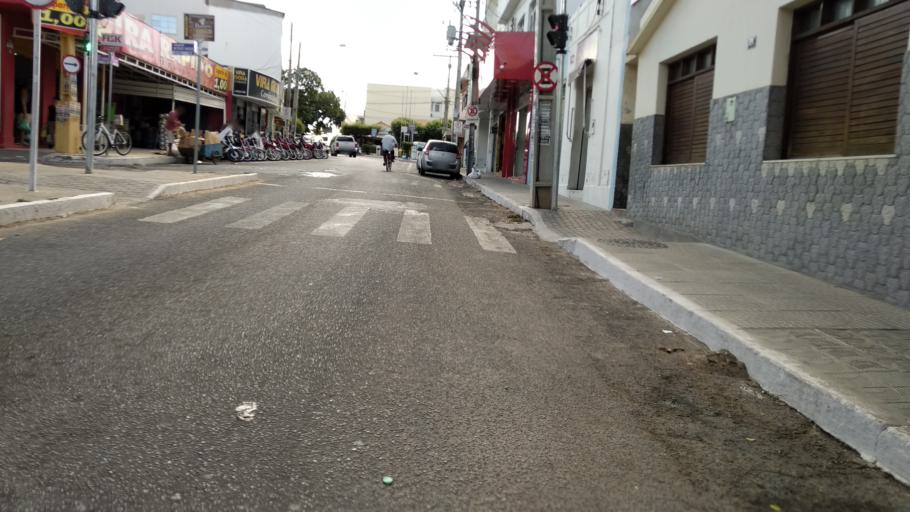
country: BR
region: Bahia
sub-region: Guanambi
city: Guanambi
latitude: -14.2286
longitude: -42.7800
